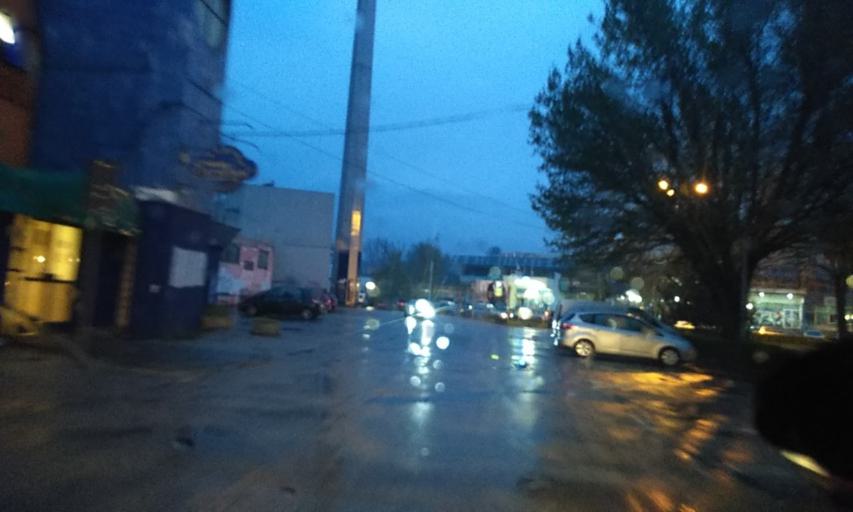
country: RS
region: Central Serbia
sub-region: Nisavski Okrug
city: Nis
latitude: 43.3153
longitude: 21.9078
